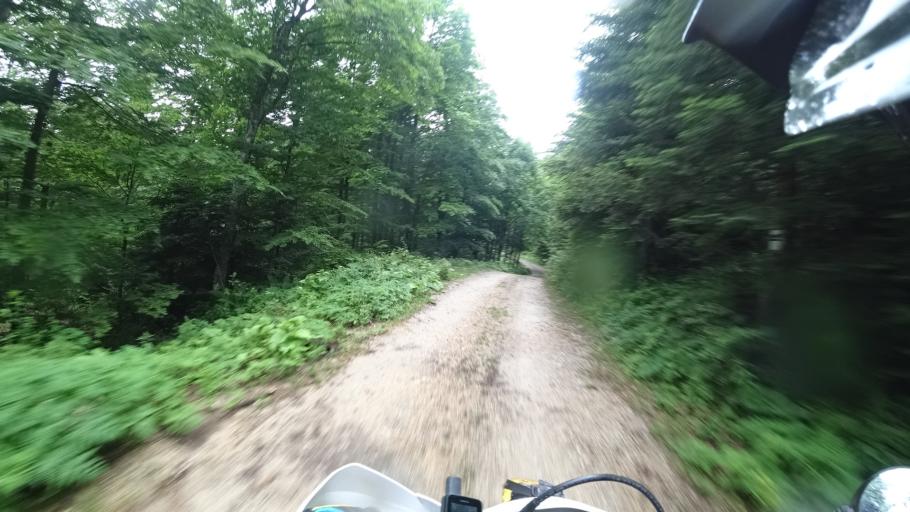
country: HR
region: Primorsko-Goranska
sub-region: Grad Delnice
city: Delnice
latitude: 45.3102
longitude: 14.9241
